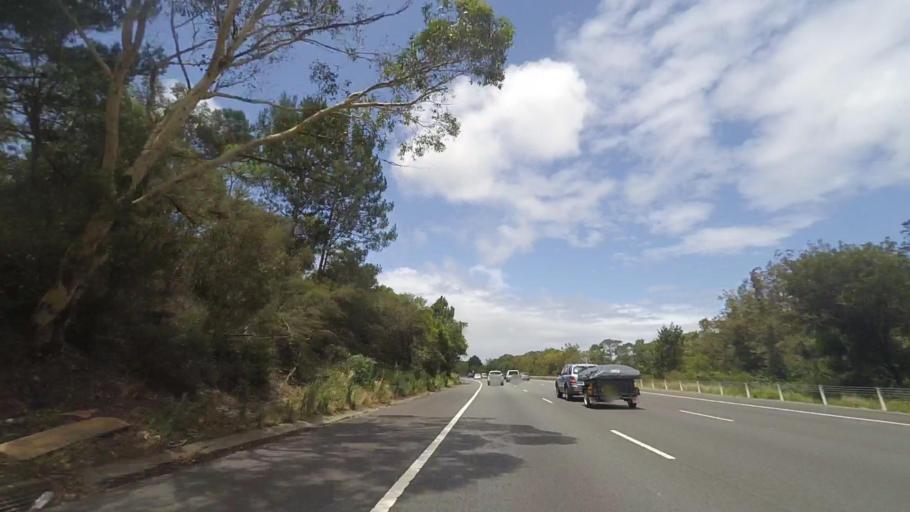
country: AU
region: New South Wales
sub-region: Gosford Shire
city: Narara
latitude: -33.3674
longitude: 151.3265
